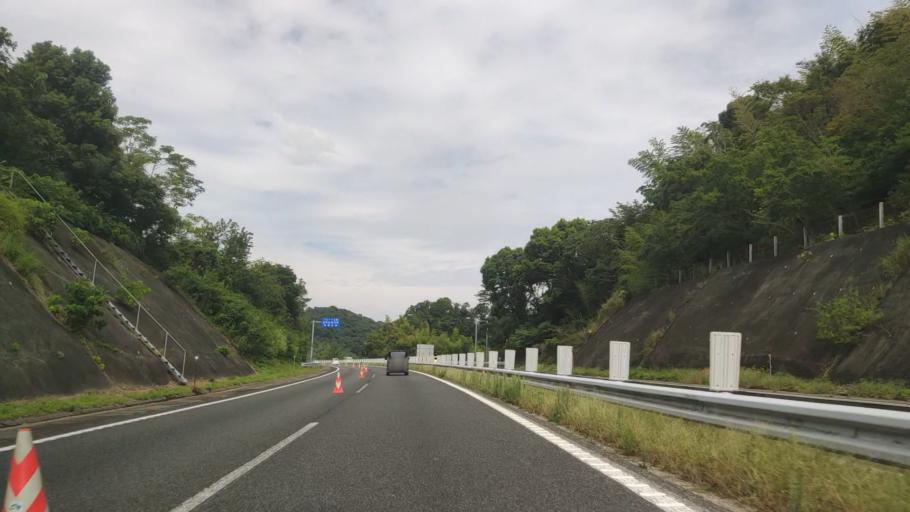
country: JP
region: Wakayama
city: Kainan
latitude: 34.1862
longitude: 135.2382
